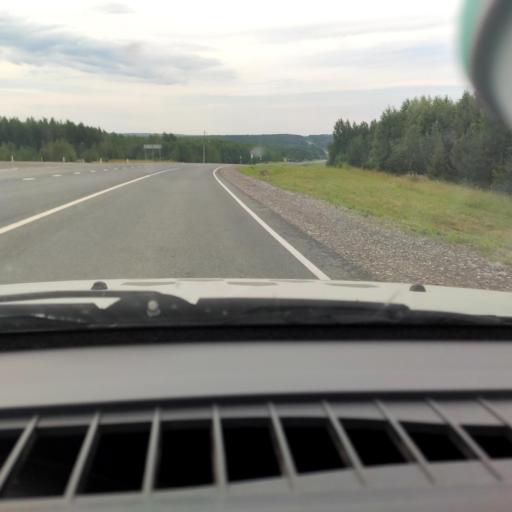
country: RU
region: Kirov
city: Kostino
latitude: 58.8108
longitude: 53.5948
